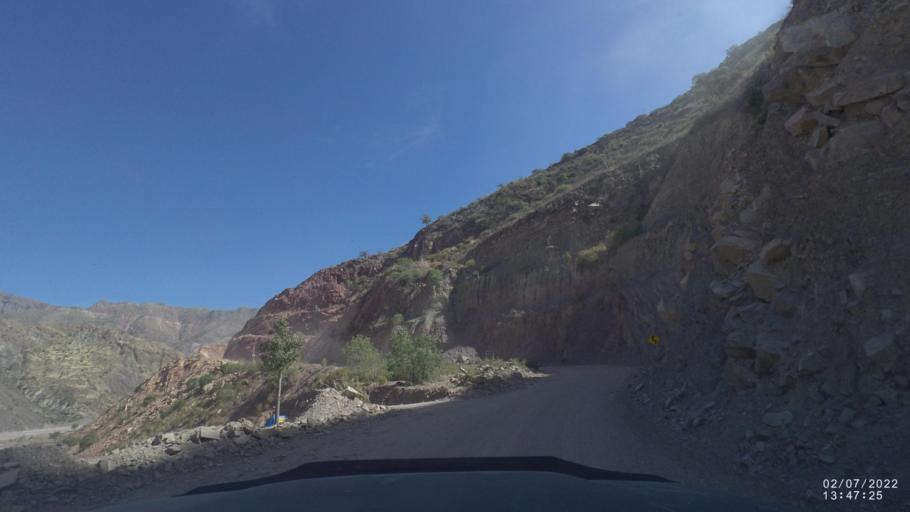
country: BO
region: Cochabamba
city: Irpa Irpa
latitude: -17.8169
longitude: -66.3701
